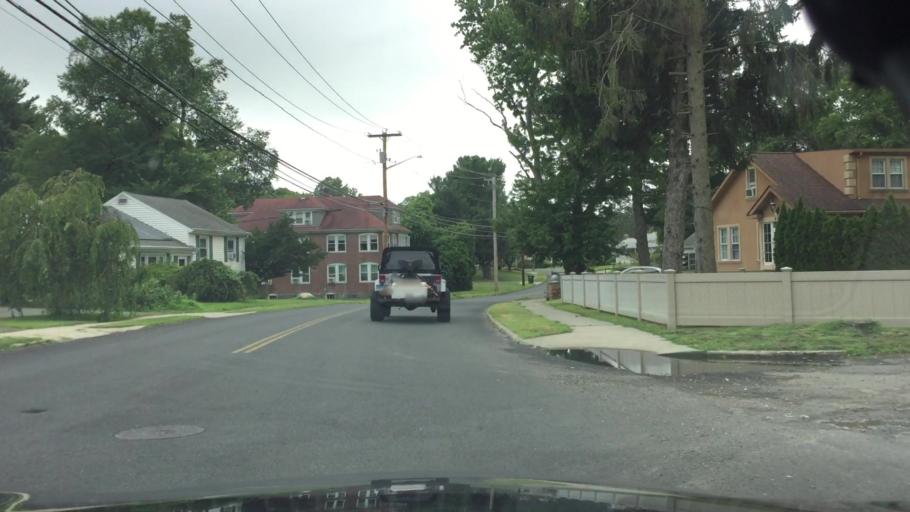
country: US
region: Connecticut
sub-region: New Haven County
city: City of Milford (balance)
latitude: 41.2005
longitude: -73.0897
